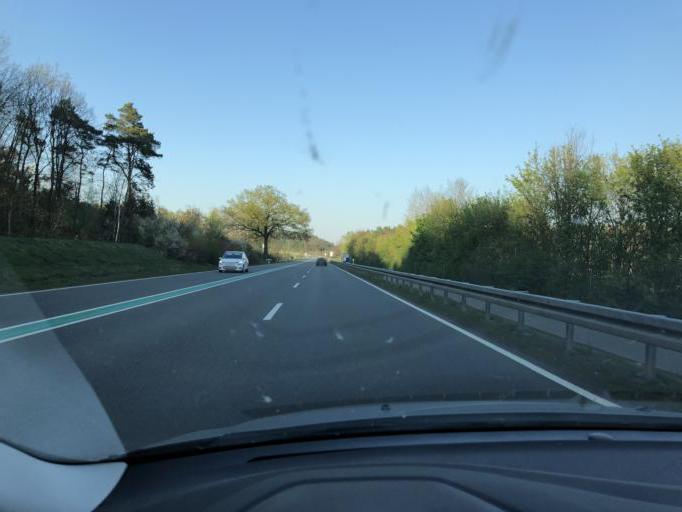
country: DE
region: Brandenburg
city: Schwarzbach
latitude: 51.4862
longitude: 13.9318
